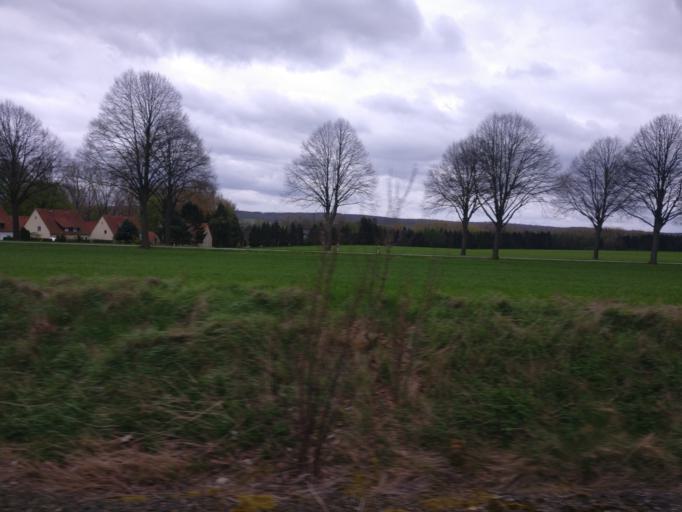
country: DE
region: Lower Saxony
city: Sehlde
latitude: 52.0518
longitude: 10.2828
